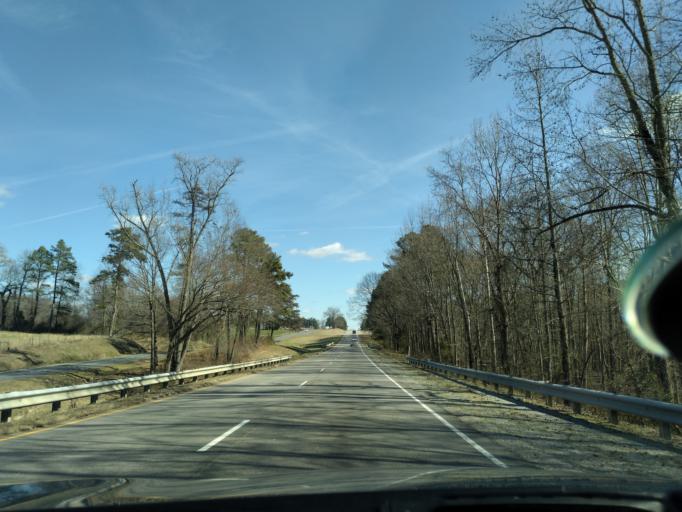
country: US
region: Virginia
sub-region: Nottoway County
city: Crewe
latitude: 37.1899
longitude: -78.1670
